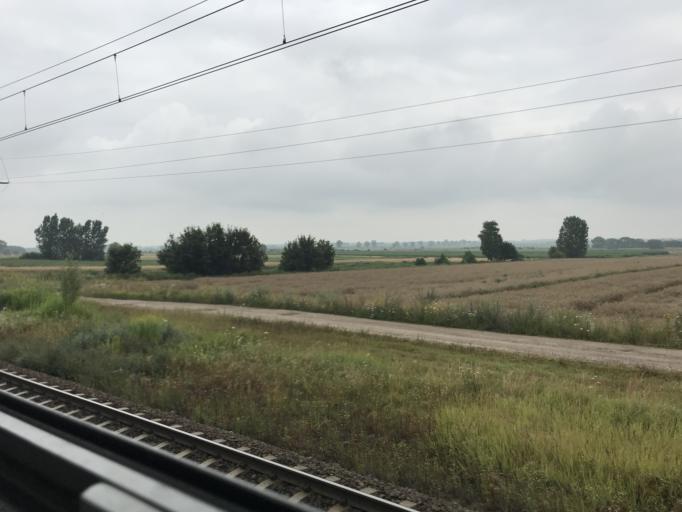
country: PL
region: Pomeranian Voivodeship
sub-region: Powiat gdanski
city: Pszczolki
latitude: 54.1989
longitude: 18.6722
